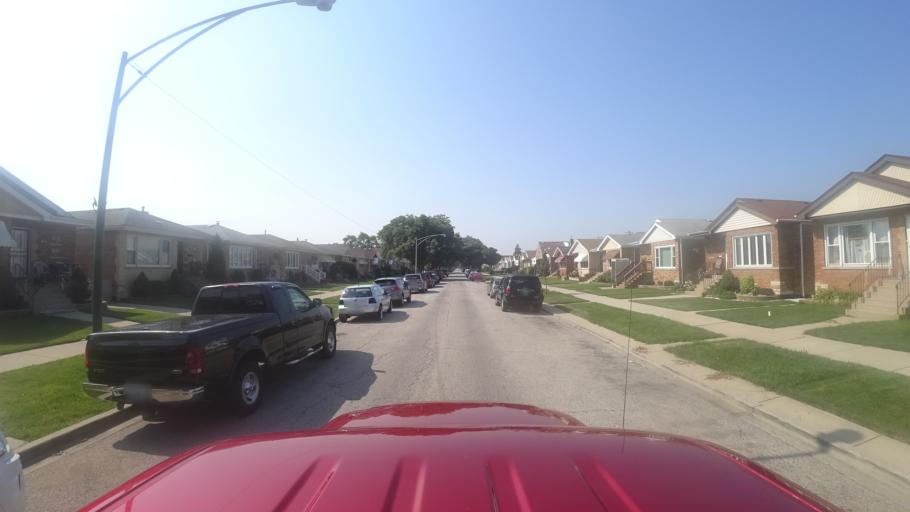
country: US
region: Illinois
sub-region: Cook County
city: Cicero
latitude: 41.8036
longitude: -87.7419
